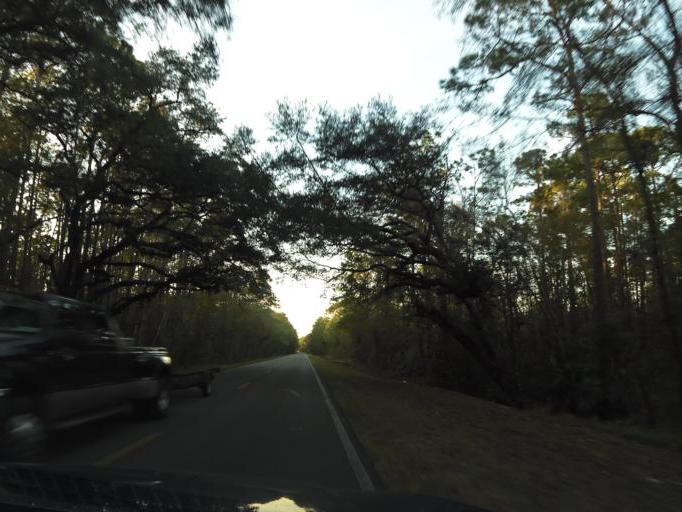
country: US
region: Florida
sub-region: Clay County
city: Green Cove Springs
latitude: 29.8874
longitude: -81.5642
